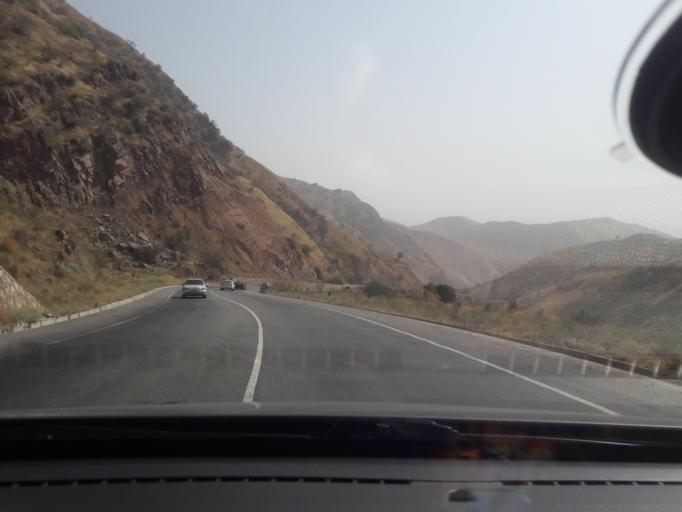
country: TJ
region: Khatlon
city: Norak
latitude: 38.4307
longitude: 69.2222
